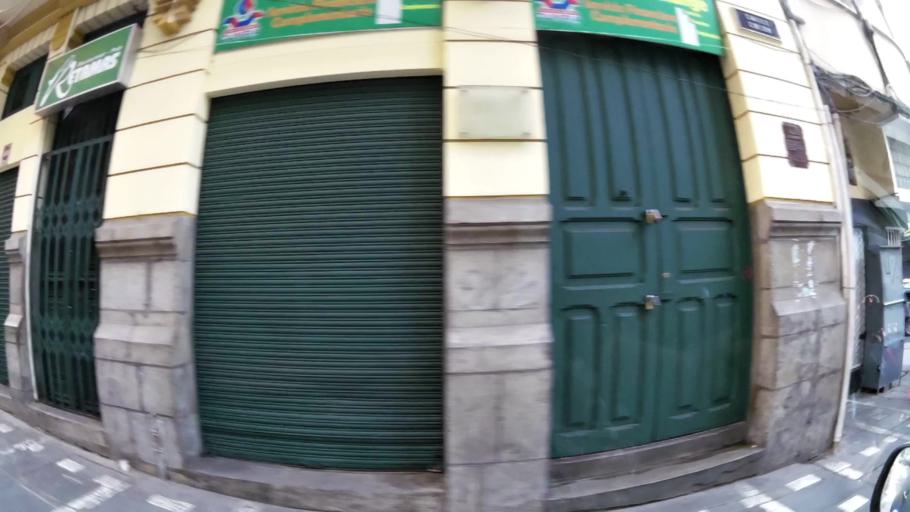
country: BO
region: La Paz
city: La Paz
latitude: -16.4988
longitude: -68.1342
